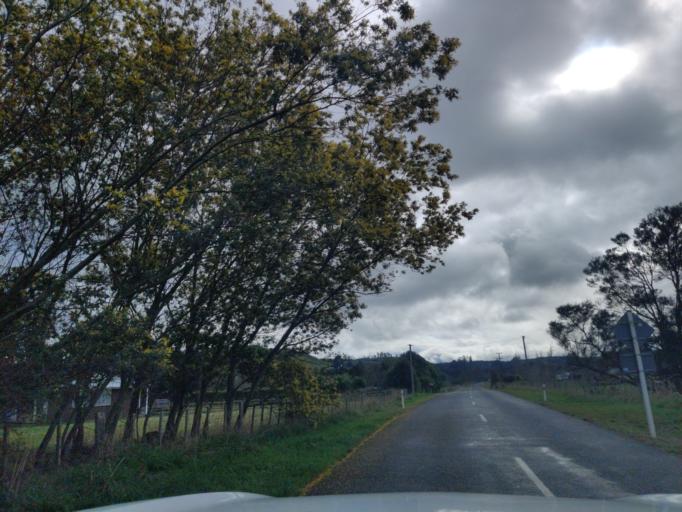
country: NZ
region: Manawatu-Wanganui
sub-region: Palmerston North City
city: Palmerston North
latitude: -40.1915
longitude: 175.7815
